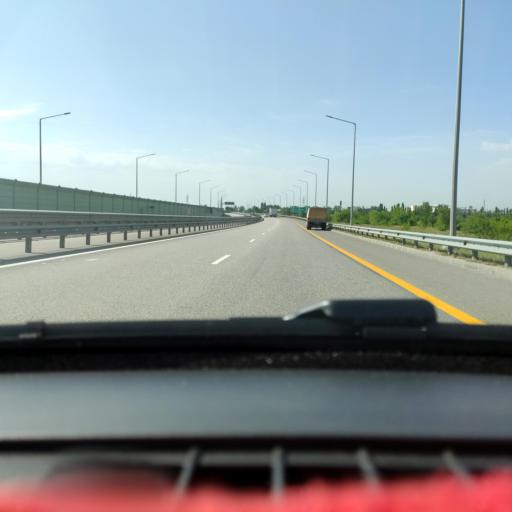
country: RU
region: Voronezj
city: Novaya Usman'
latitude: 51.6365
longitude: 39.3165
